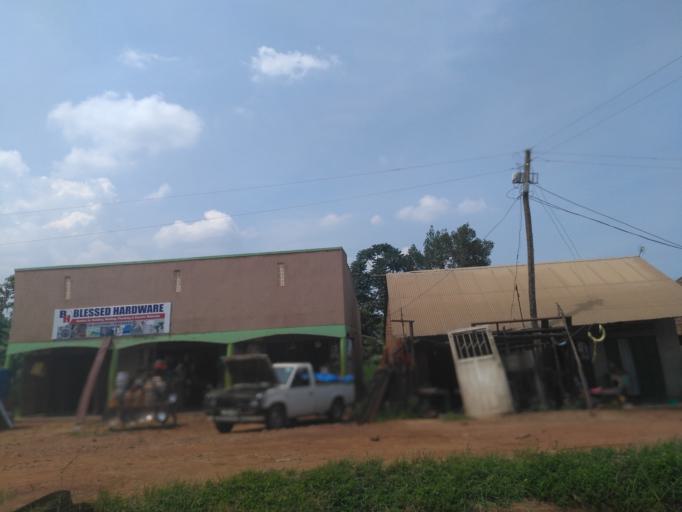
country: UG
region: Central Region
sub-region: Wakiso District
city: Kireka
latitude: 0.4559
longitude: 32.6060
